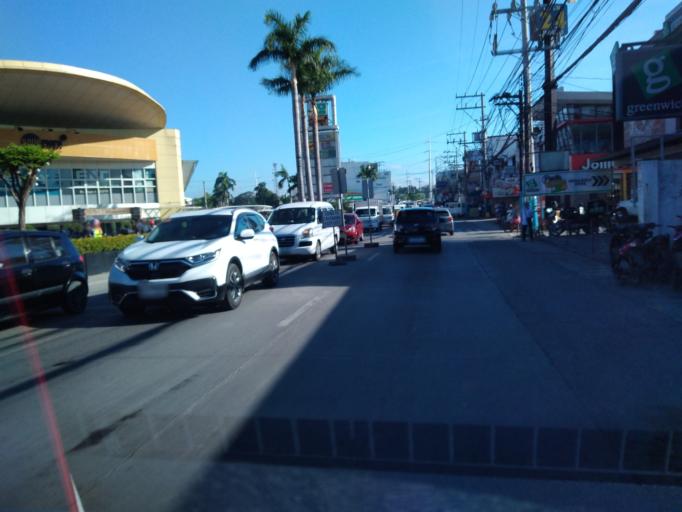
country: PH
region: Central Luzon
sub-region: Province of Bulacan
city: Meycauayan
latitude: 14.7433
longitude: 120.9707
